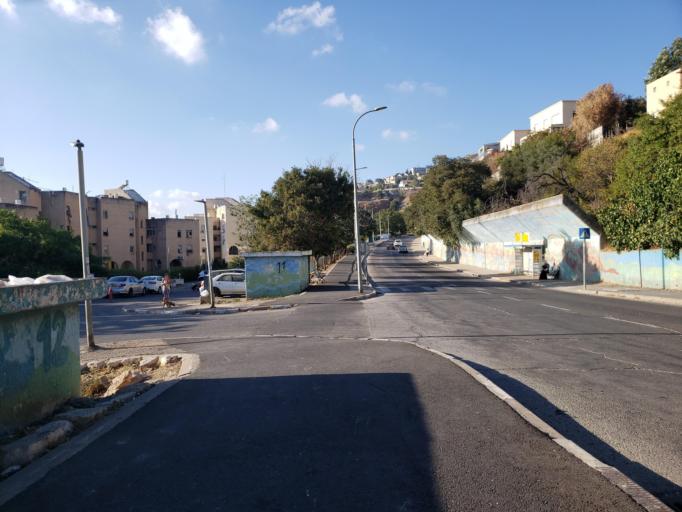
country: IL
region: Northern District
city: Safed
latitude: 32.9606
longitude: 35.4915
